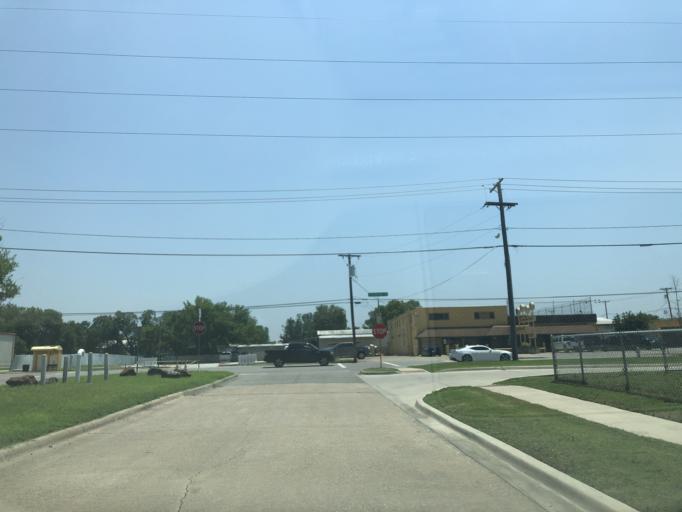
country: US
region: Texas
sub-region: Dallas County
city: Dallas
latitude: 32.7790
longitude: -96.8348
